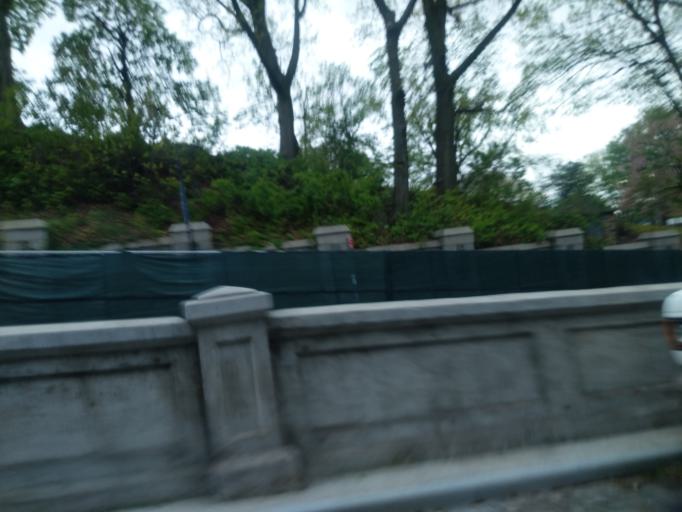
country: US
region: New Jersey
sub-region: Bergen County
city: Fort Lee
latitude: 40.8334
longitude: -73.9472
